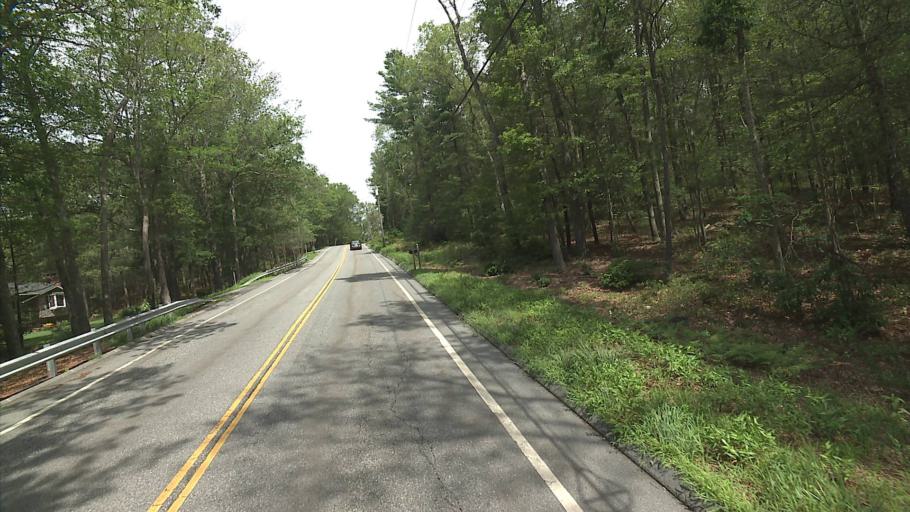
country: US
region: Connecticut
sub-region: Windham County
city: Putnam
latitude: 41.8896
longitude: -71.8679
